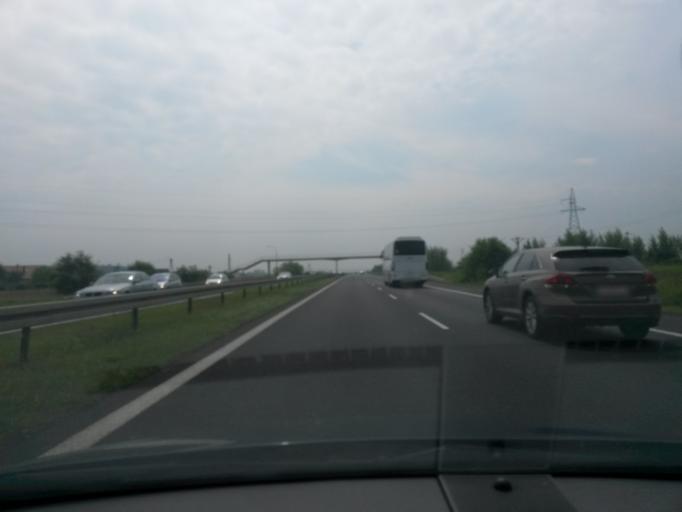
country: PL
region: Lodz Voivodeship
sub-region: Powiat piotrkowski
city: Wola Krzysztoporska
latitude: 51.3422
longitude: 19.5971
